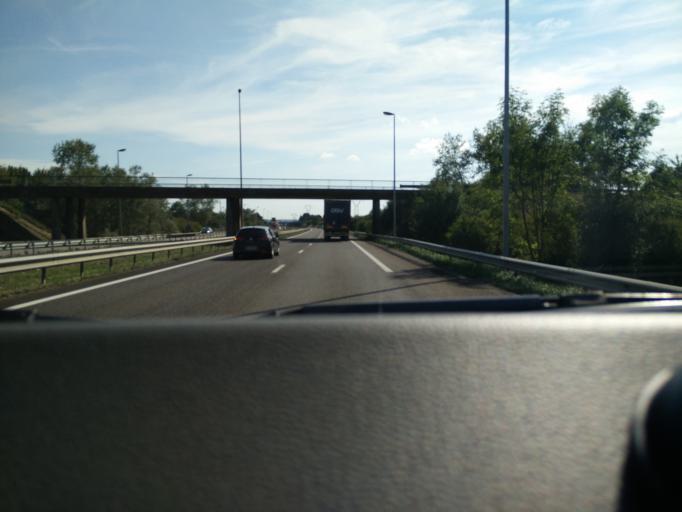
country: FR
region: Lorraine
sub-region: Departement de Meurthe-et-Moselle
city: Pont-a-Mousson
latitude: 48.8908
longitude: 6.0999
